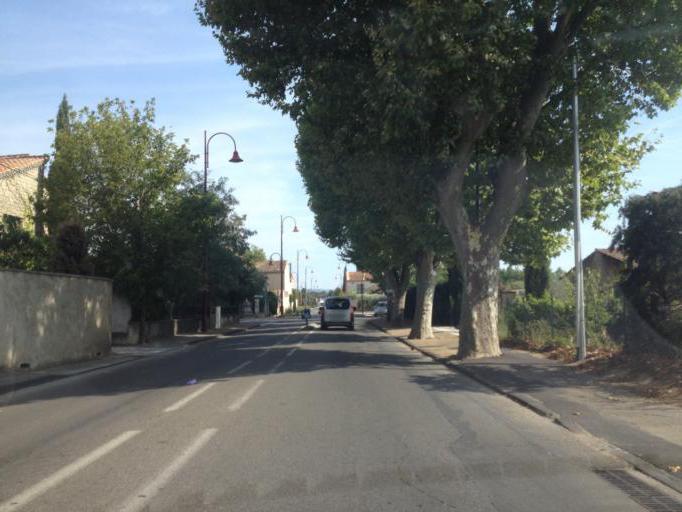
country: FR
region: Provence-Alpes-Cote d'Azur
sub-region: Departement du Vaucluse
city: Aubignan
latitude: 44.0963
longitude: 5.0262
